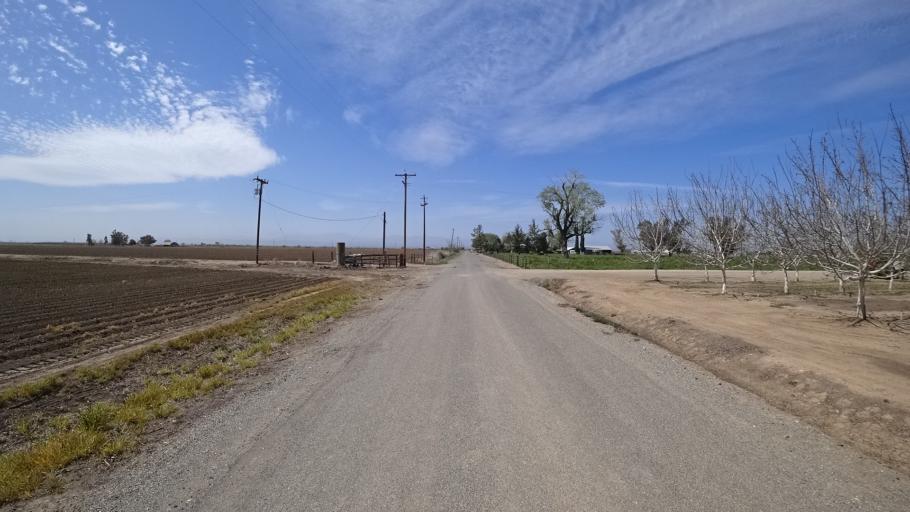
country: US
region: California
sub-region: Glenn County
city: Willows
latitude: 39.5733
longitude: -122.1981
